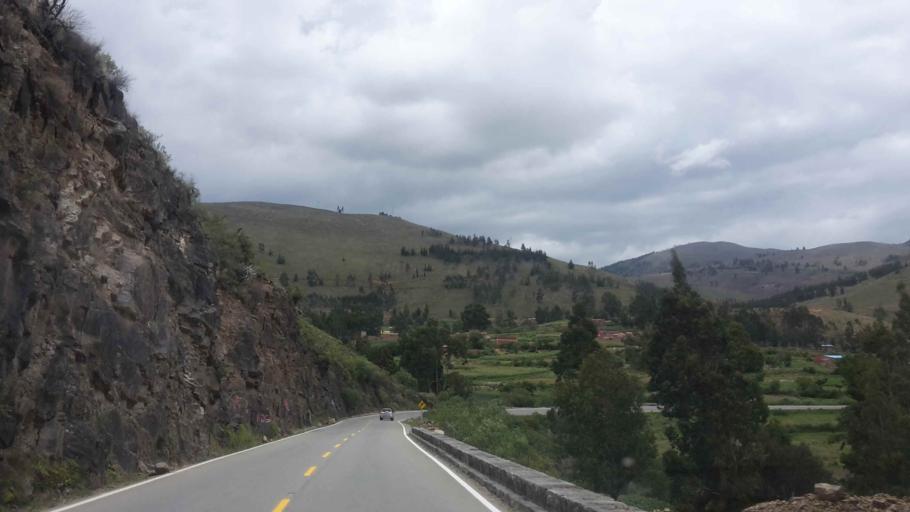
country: BO
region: Cochabamba
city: Arani
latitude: -17.4769
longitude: -65.7643
